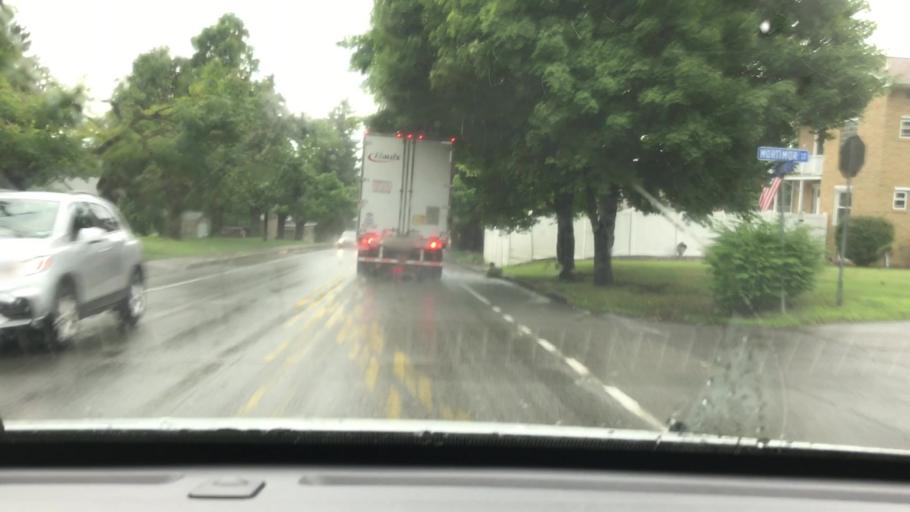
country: US
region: Pennsylvania
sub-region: Centre County
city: Philipsburg
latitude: 40.8897
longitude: -78.2142
